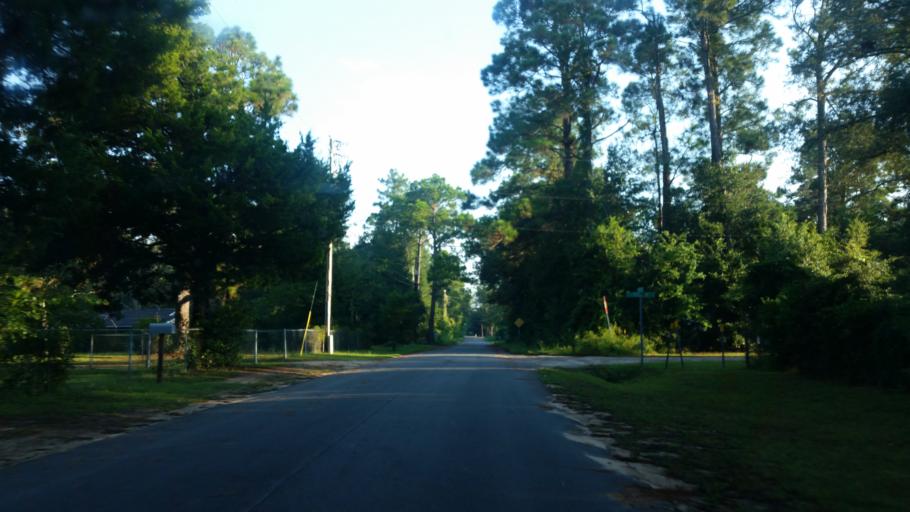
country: US
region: Florida
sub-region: Santa Rosa County
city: East Milton
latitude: 30.6274
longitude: -87.0195
